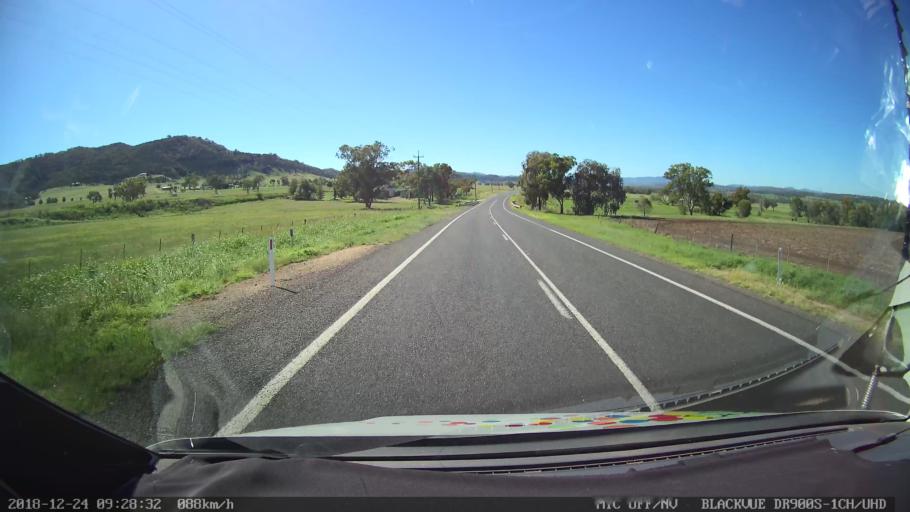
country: AU
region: New South Wales
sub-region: Liverpool Plains
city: Quirindi
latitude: -31.5390
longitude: 150.6896
